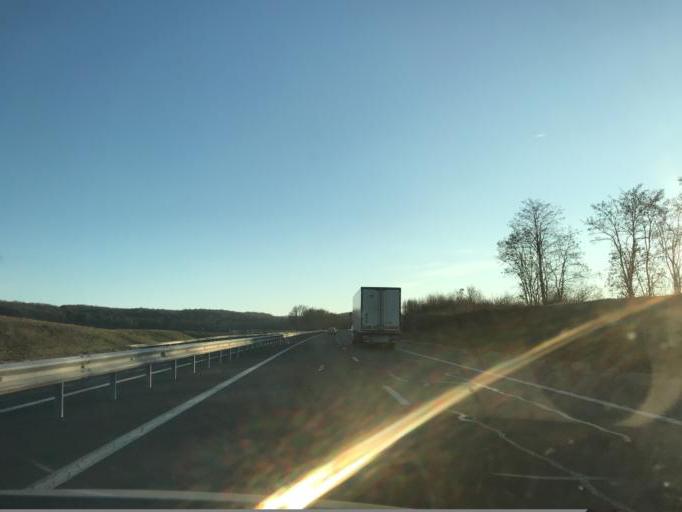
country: FR
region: Bourgogne
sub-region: Departement de l'Yonne
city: Saint-Martin-du-Tertre
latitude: 48.2197
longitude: 3.2366
